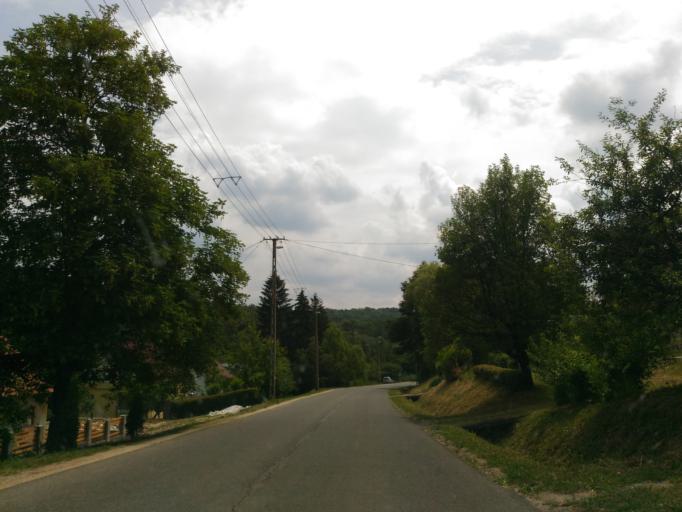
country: HU
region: Baranya
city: Komlo
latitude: 46.1793
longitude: 18.2315
